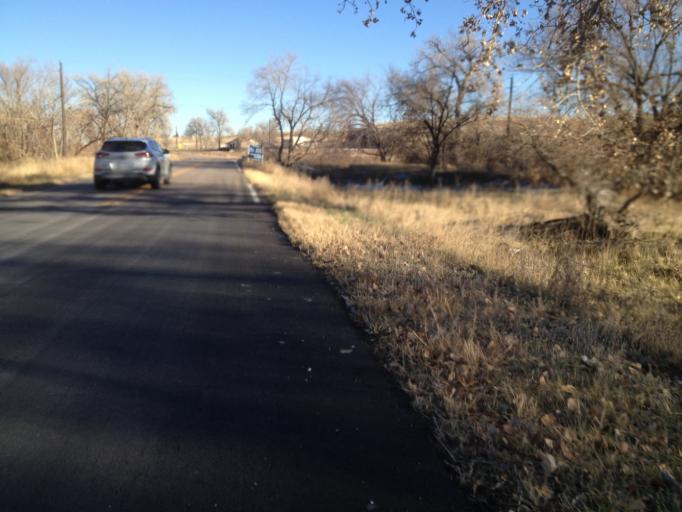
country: US
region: Colorado
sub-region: Boulder County
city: Louisville
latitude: 39.9764
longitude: -105.1175
